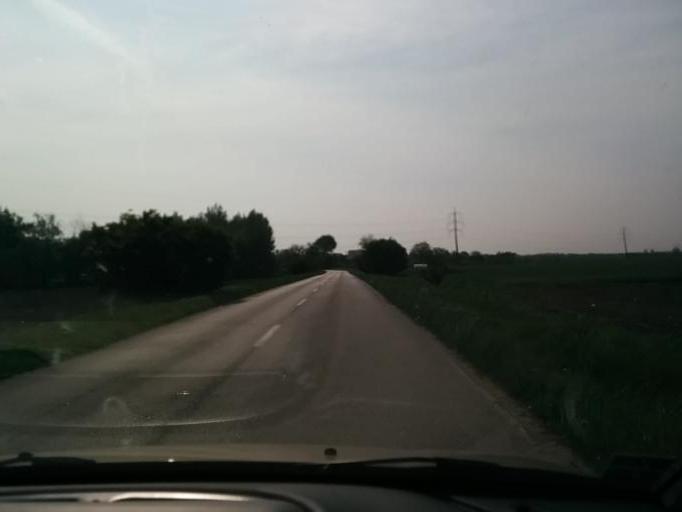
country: SK
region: Trnavsky
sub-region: Okres Galanta
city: Galanta
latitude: 48.2343
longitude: 17.7103
